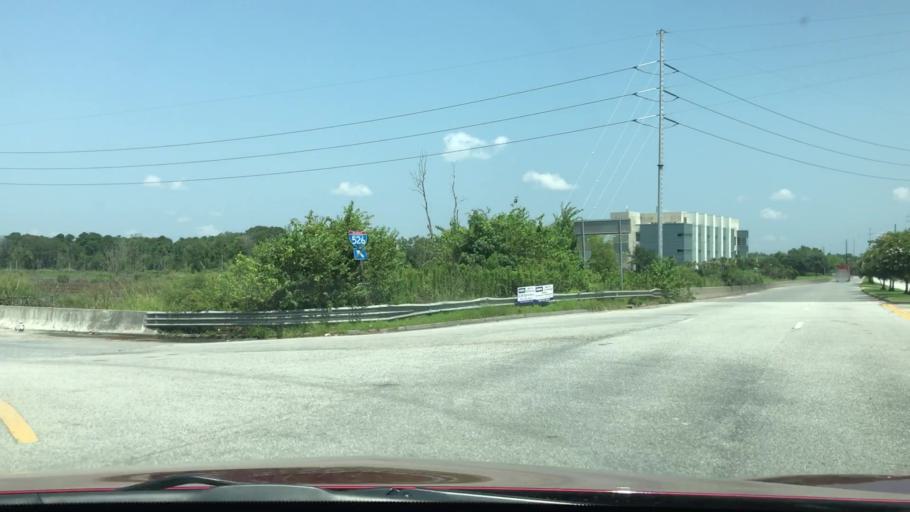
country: US
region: South Carolina
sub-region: Charleston County
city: North Charleston
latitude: 32.8934
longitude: -79.9730
